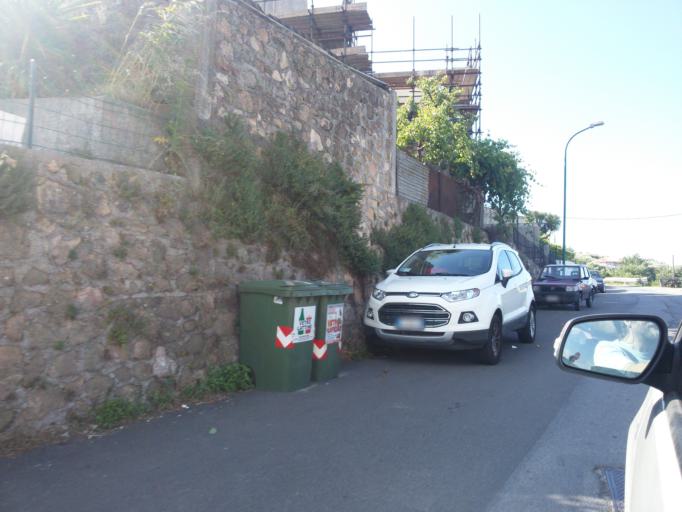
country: IT
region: Liguria
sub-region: Provincia di Savona
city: Borgio
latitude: 44.1793
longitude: 8.3031
